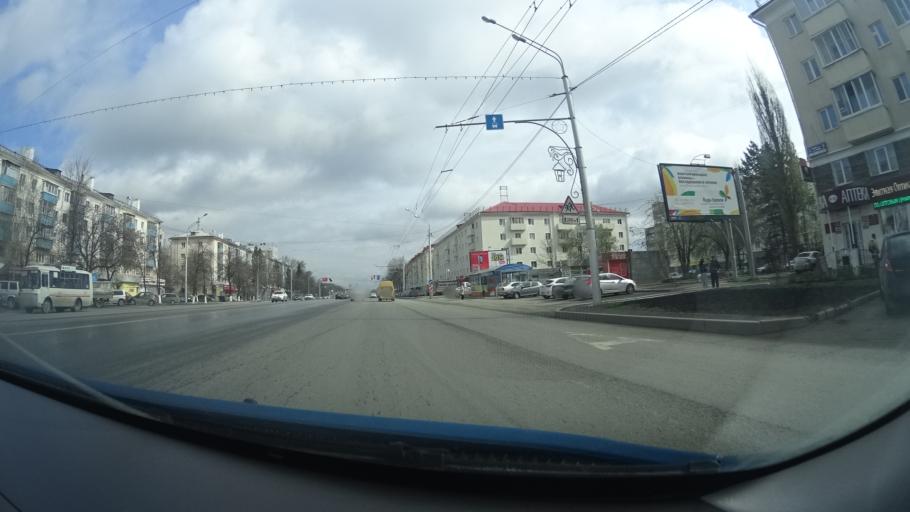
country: RU
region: Bashkortostan
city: Ufa
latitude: 54.7430
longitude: 55.9862
